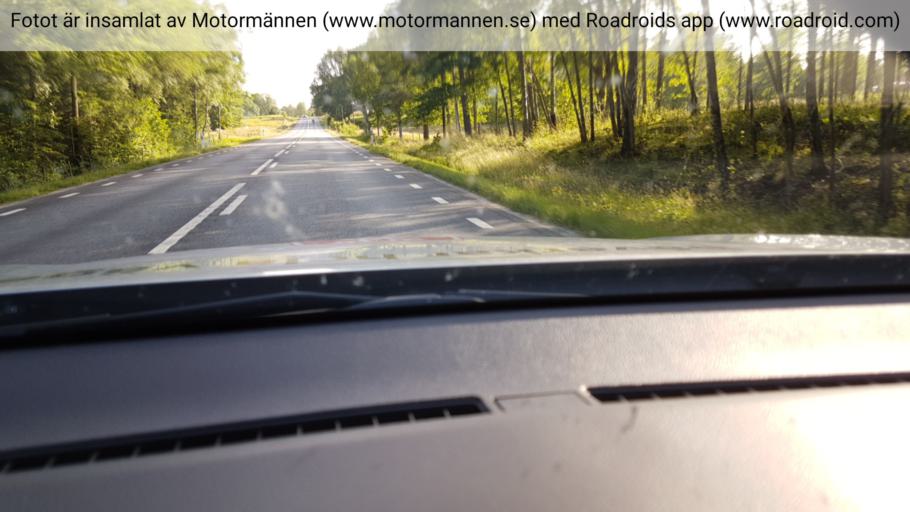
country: SE
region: Joenkoeping
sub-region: Varnamo Kommun
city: Varnamo
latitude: 57.2240
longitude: 14.1176
